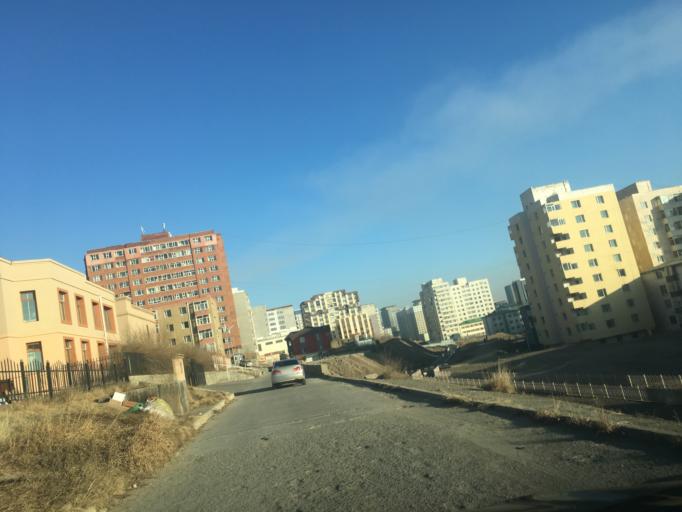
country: MN
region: Ulaanbaatar
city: Ulaanbaatar
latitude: 47.9174
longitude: 106.8794
